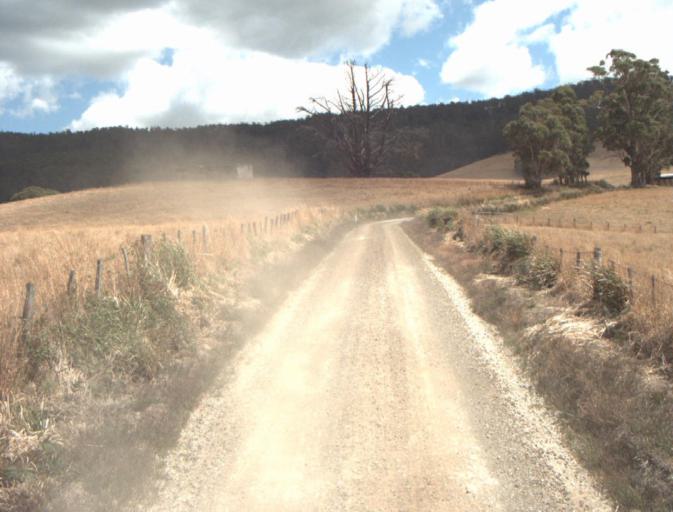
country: AU
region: Tasmania
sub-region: Launceston
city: Mayfield
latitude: -41.2263
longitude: 147.1191
